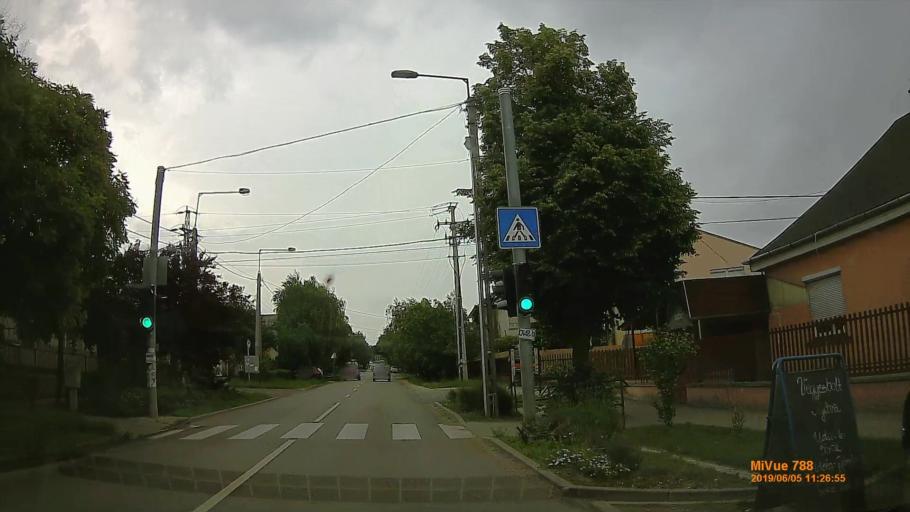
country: HU
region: Pest
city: Maglod
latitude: 47.4456
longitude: 19.3576
